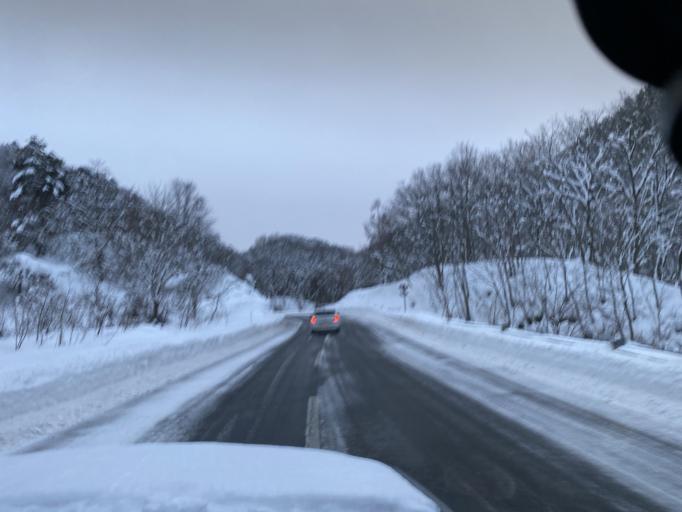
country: JP
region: Nagano
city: Omachi
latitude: 36.5899
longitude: 137.8886
